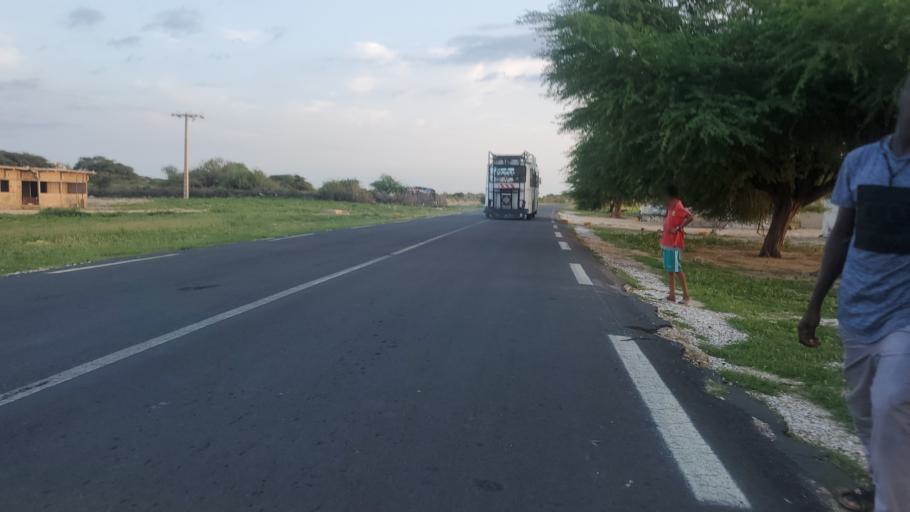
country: SN
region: Saint-Louis
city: Saint-Louis
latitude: 16.1418
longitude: -16.4097
